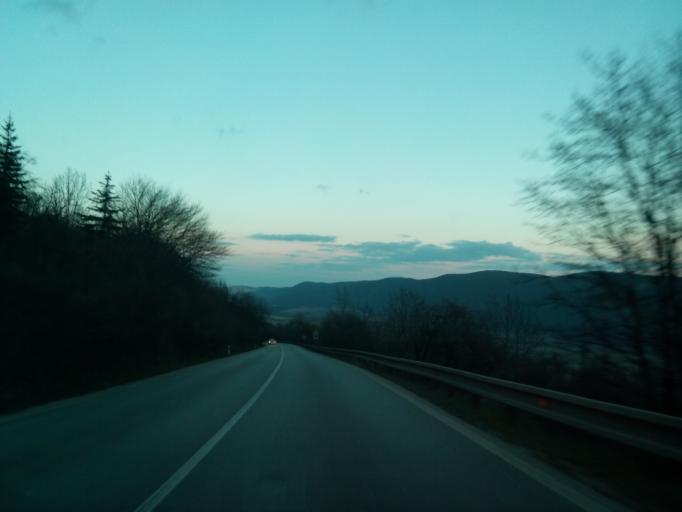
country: SK
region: Kosicky
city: Roznava
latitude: 48.6009
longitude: 20.6504
